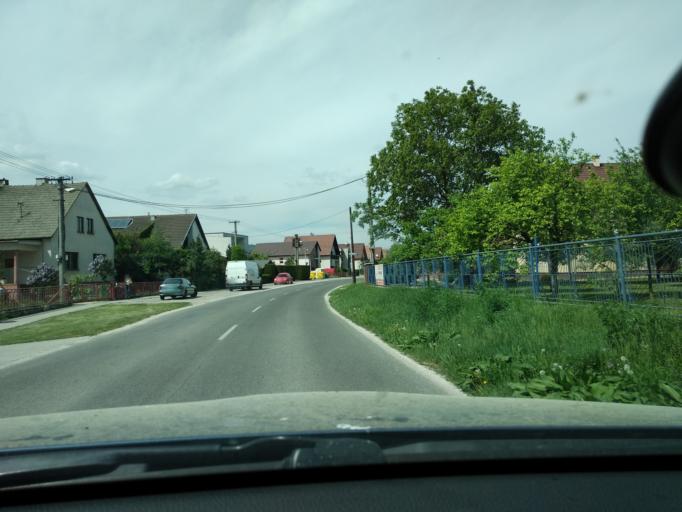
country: SK
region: Trenciansky
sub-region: Okres Nove Mesto nad Vahom
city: Nove Mesto nad Vahom
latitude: 48.7993
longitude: 17.8593
